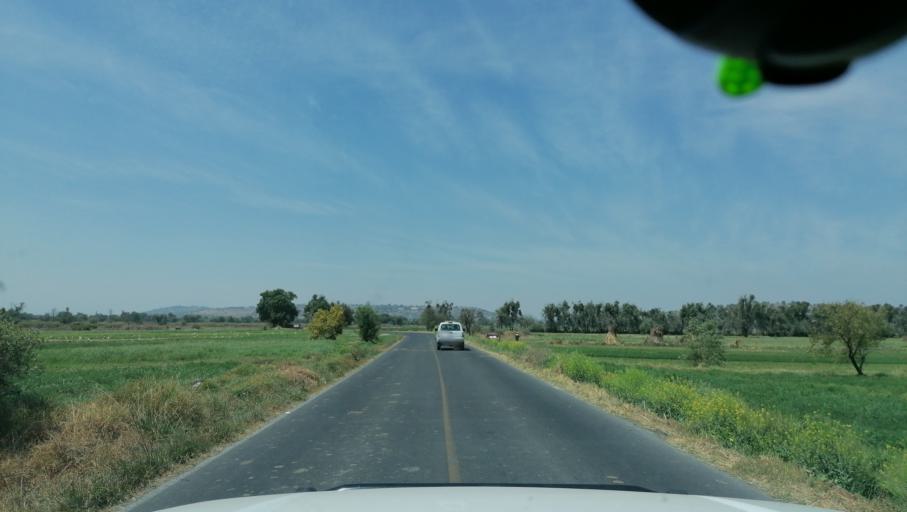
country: MX
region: Tlaxcala
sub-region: Tetlatlahuca
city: Tetlatlahuca
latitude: 19.2145
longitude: -98.2857
